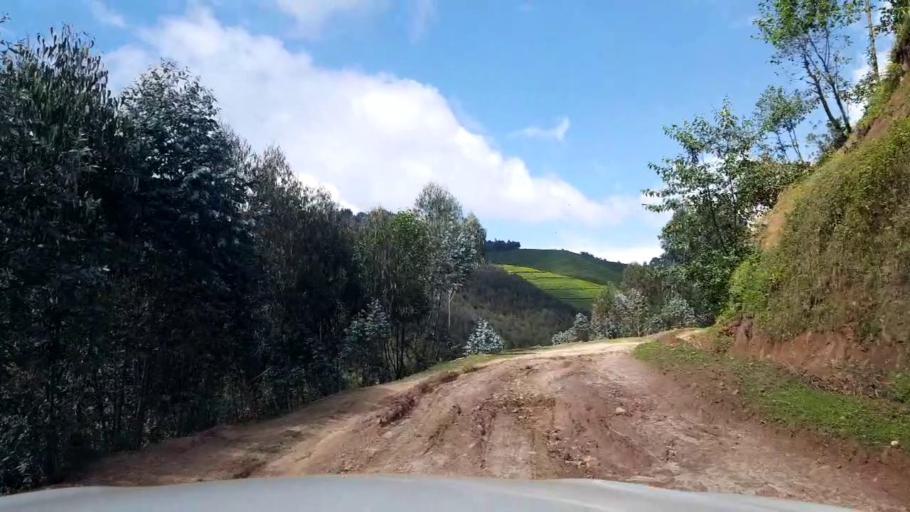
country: RW
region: Western Province
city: Kibuye
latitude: -1.8820
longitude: 29.4687
